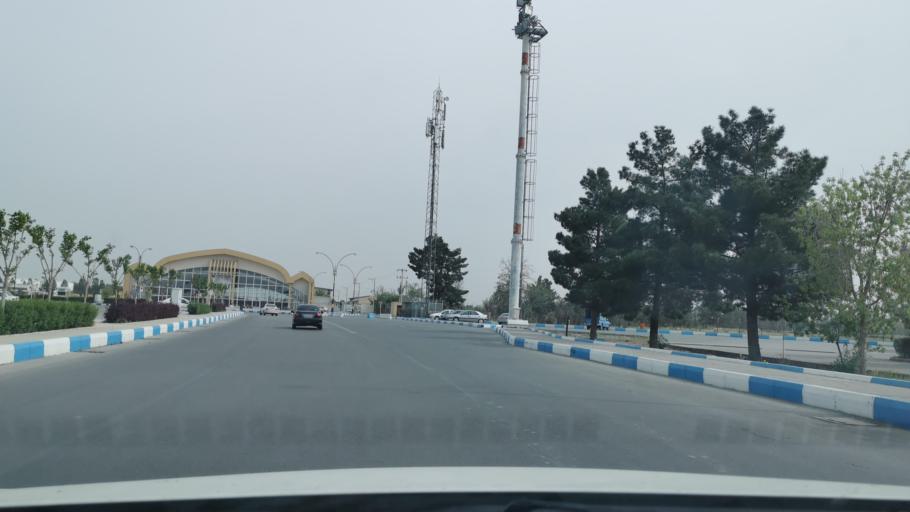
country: IR
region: Razavi Khorasan
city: Mashhad
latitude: 36.2262
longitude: 59.6395
